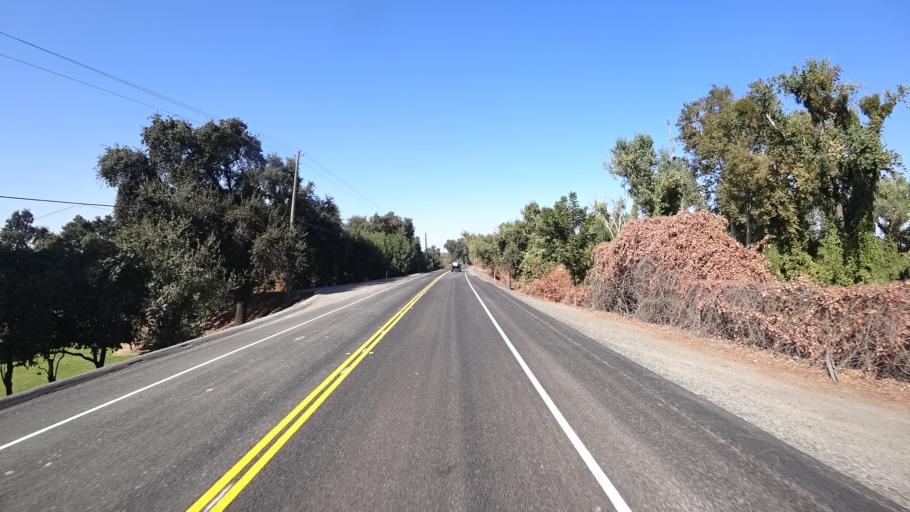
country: US
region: California
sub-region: Yolo County
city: West Sacramento
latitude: 38.6552
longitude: -121.6066
